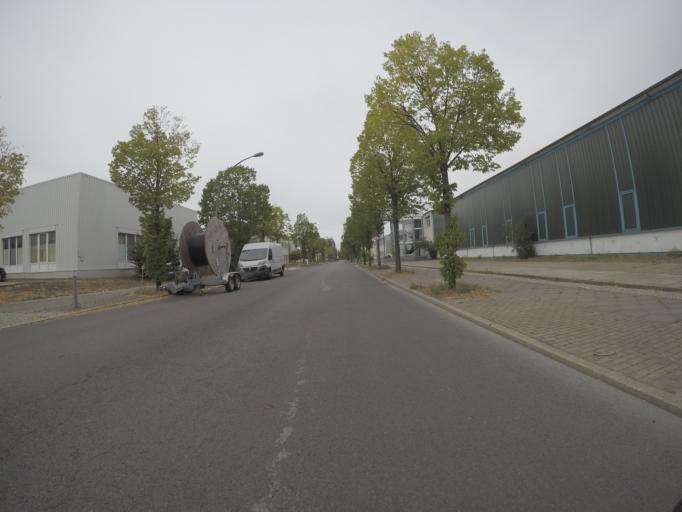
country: DE
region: Berlin
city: Alt-Hohenschoenhausen
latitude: 52.5417
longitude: 13.5232
